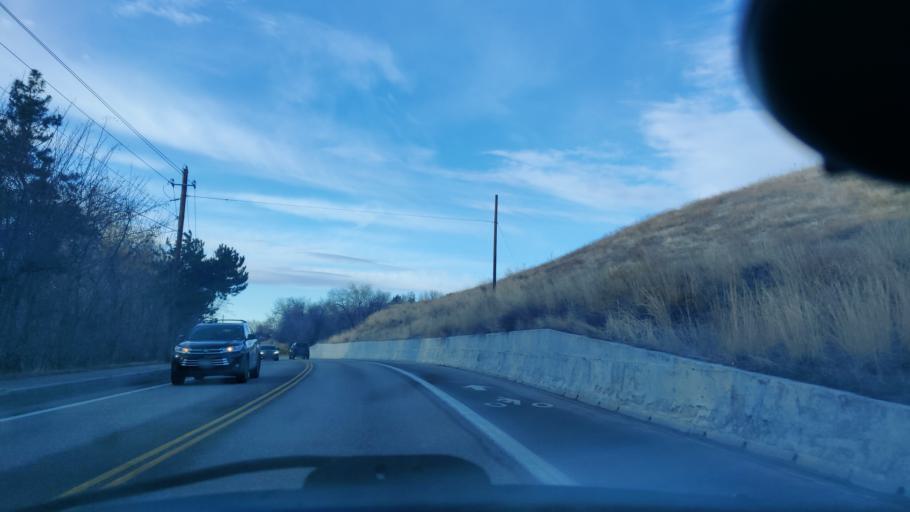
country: US
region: Idaho
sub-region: Ada County
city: Garden City
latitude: 43.6509
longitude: -116.2261
